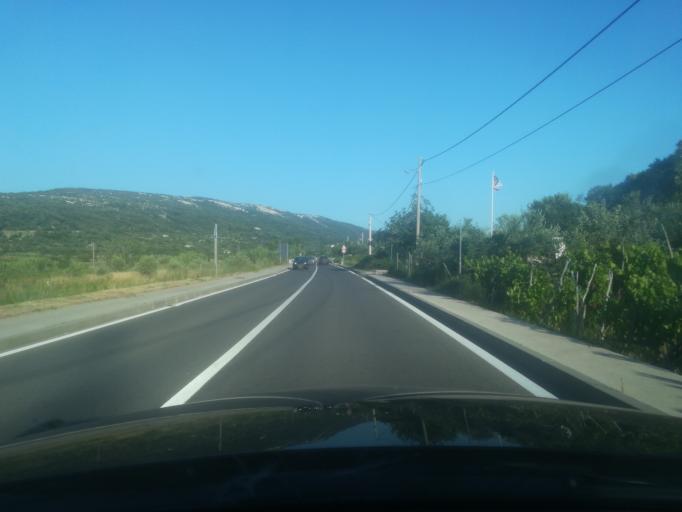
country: HR
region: Primorsko-Goranska
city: Supetarska Draga
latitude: 44.7869
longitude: 14.7418
